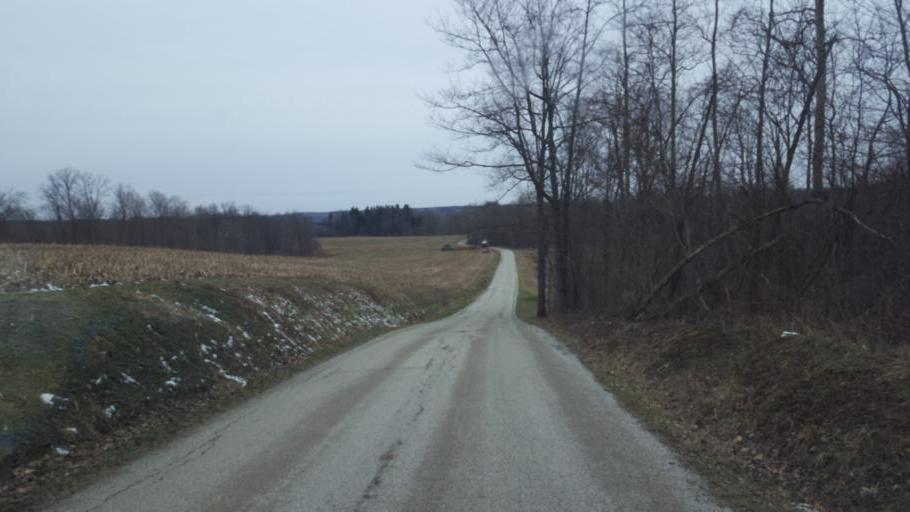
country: US
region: Ohio
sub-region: Sandusky County
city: Bellville
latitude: 40.5874
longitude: -82.4856
